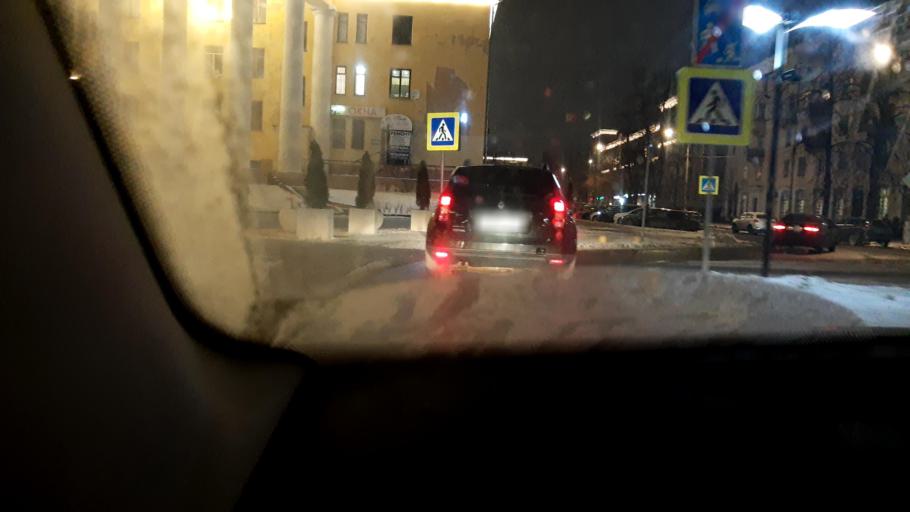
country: RU
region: Moskovskaya
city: Elektrostal'
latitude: 55.7893
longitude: 38.4431
